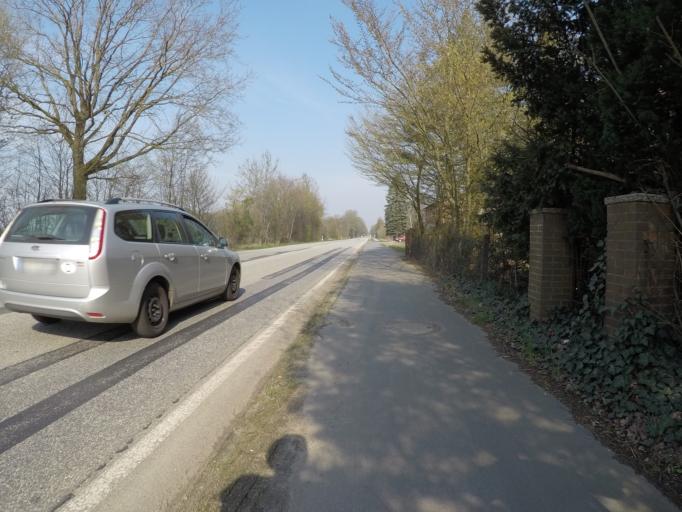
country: DE
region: Schleswig-Holstein
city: Gross Niendorf
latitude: 53.8361
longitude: 10.2206
